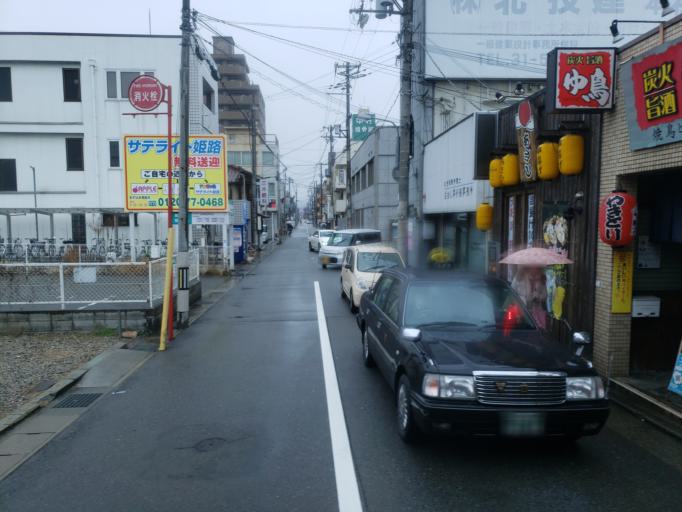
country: JP
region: Hyogo
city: Himeji
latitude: 34.8003
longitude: 134.6744
